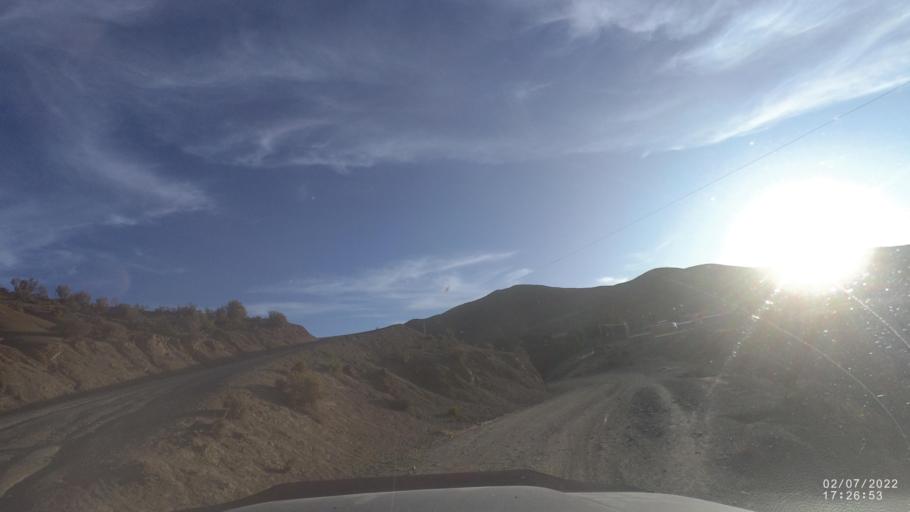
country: BO
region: Cochabamba
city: Irpa Irpa
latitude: -17.8821
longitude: -66.6140
